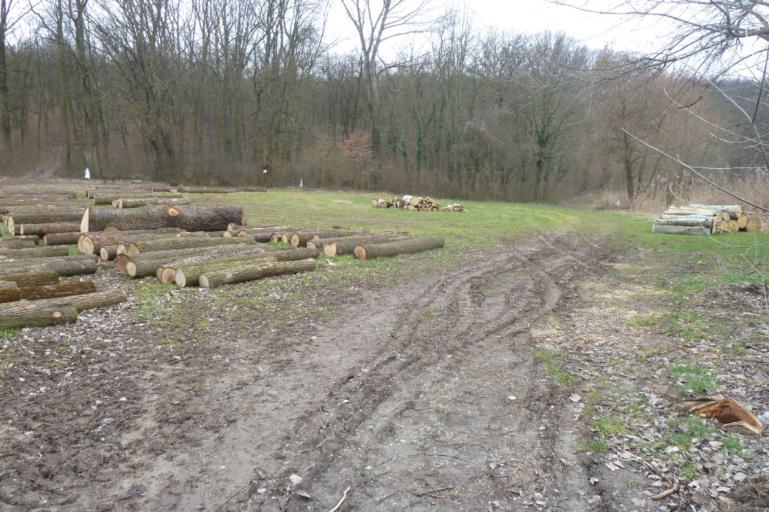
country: HU
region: Pest
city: Vacszentlaszlo
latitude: 47.6021
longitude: 19.5324
